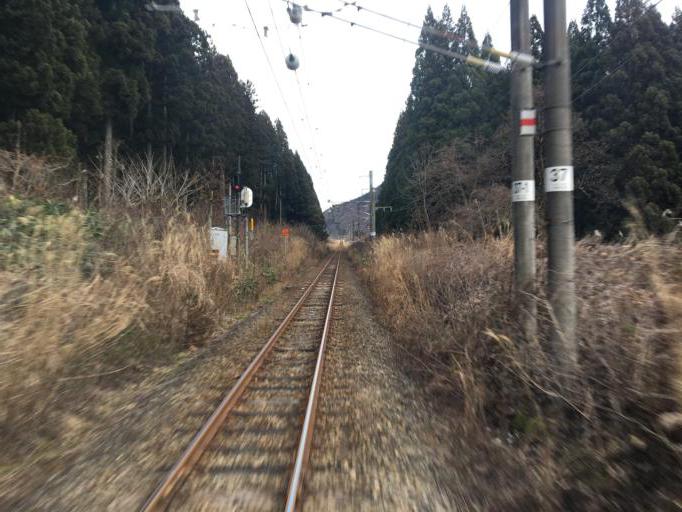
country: JP
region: Yamagata
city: Shinjo
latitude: 38.9511
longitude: 140.2762
